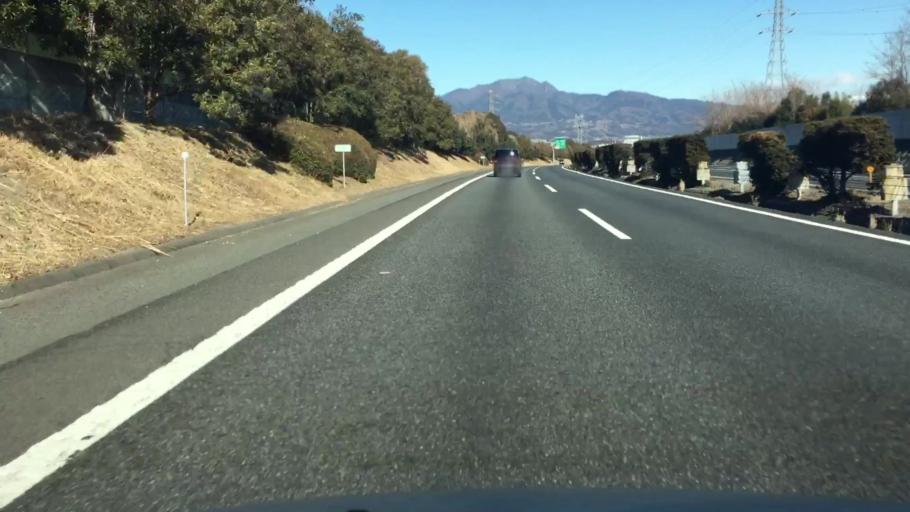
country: JP
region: Gunma
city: Shibukawa
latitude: 36.4626
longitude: 139.0116
